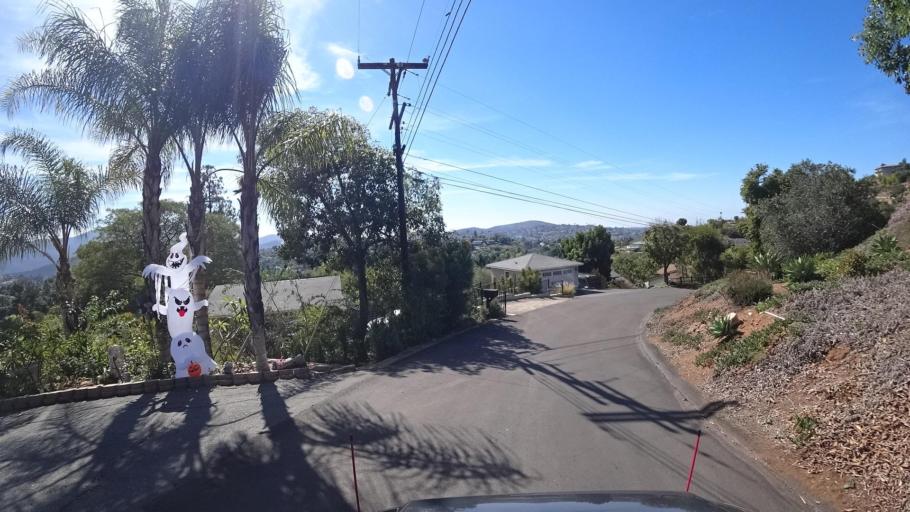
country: US
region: California
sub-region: San Diego County
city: Casa de Oro-Mount Helix
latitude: 32.7581
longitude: -116.9675
